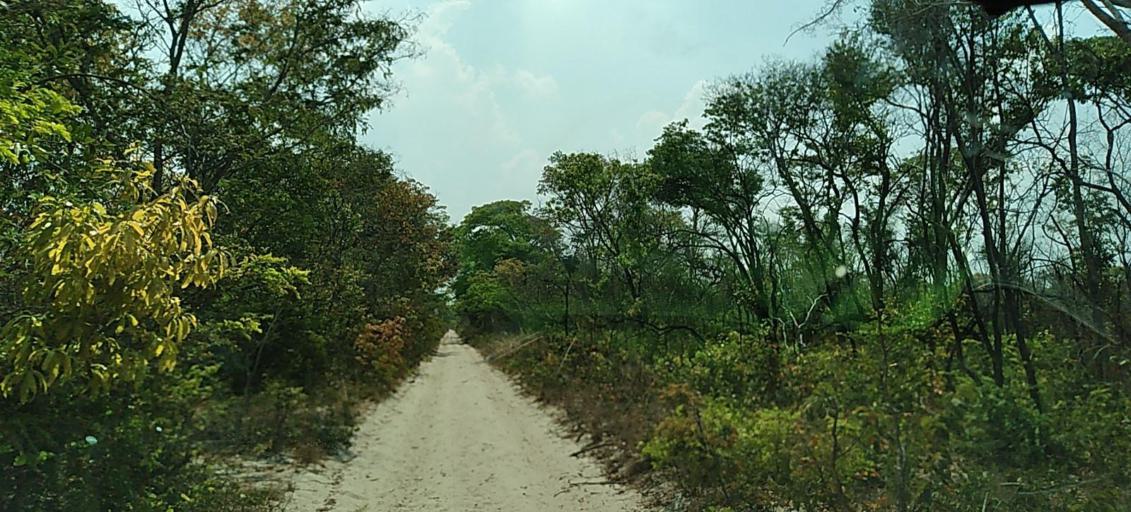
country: ZM
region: North-Western
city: Kabompo
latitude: -13.3972
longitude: 23.8022
